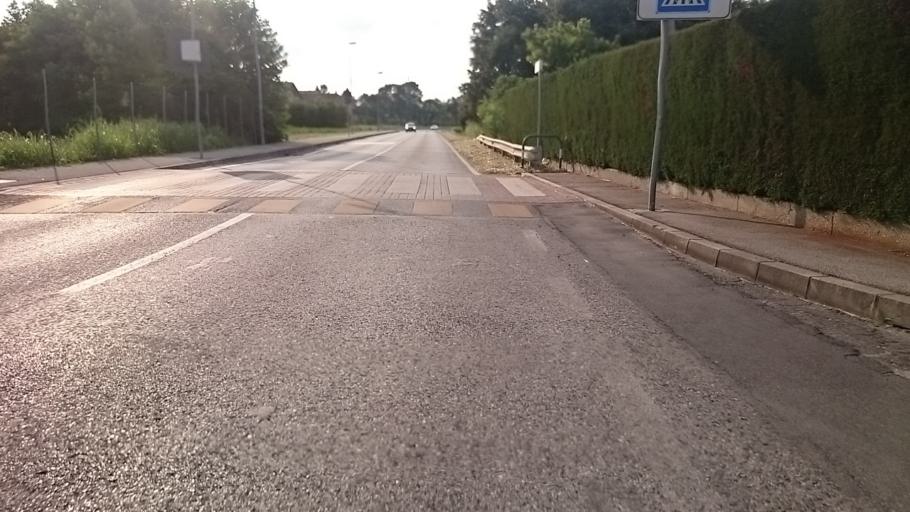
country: IT
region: Veneto
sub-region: Provincia di Padova
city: Ponte San Nicolo
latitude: 45.3744
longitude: 11.9390
